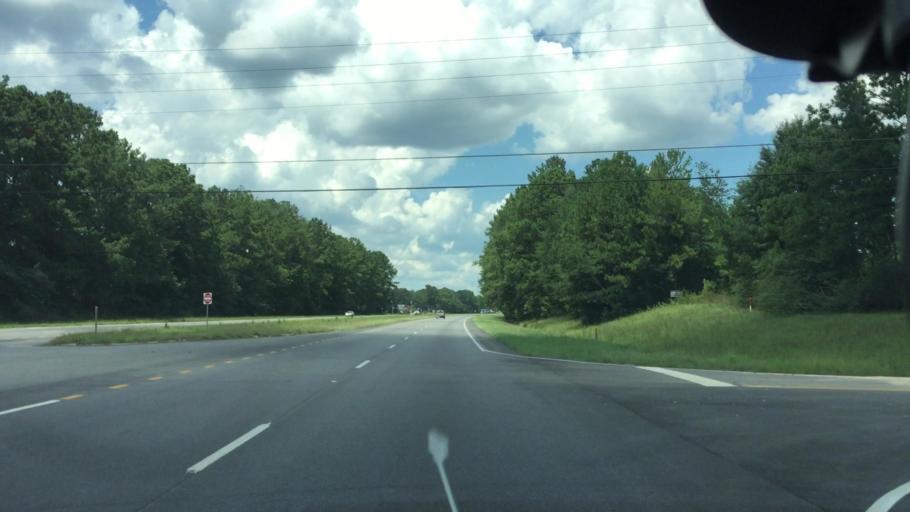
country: US
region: Alabama
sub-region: Pike County
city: Troy
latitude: 31.8906
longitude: -86.0085
